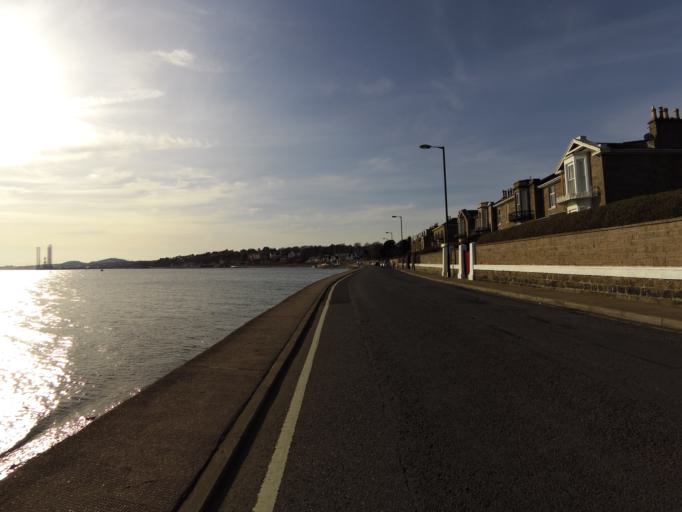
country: GB
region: Scotland
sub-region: Fife
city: Tayport
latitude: 56.4668
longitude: -2.8833
